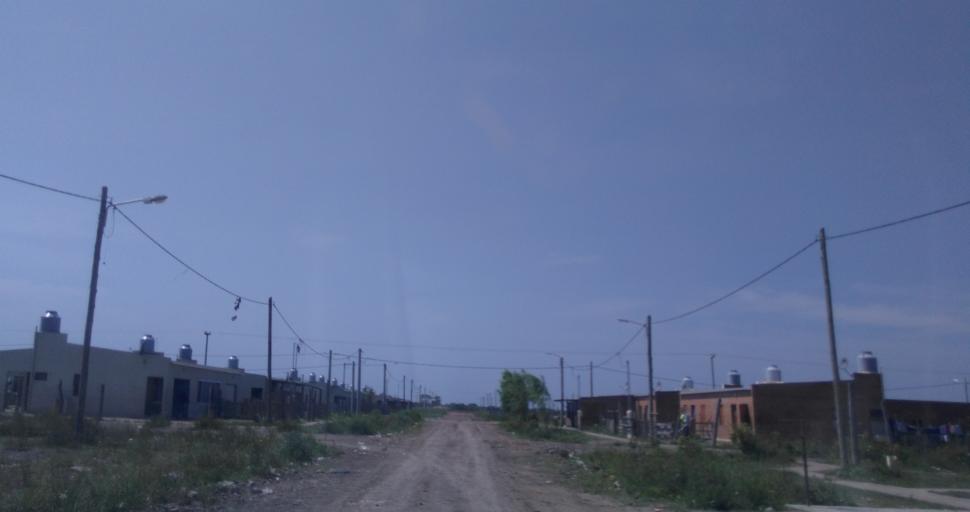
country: AR
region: Chaco
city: Fontana
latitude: -27.3974
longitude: -58.9892
